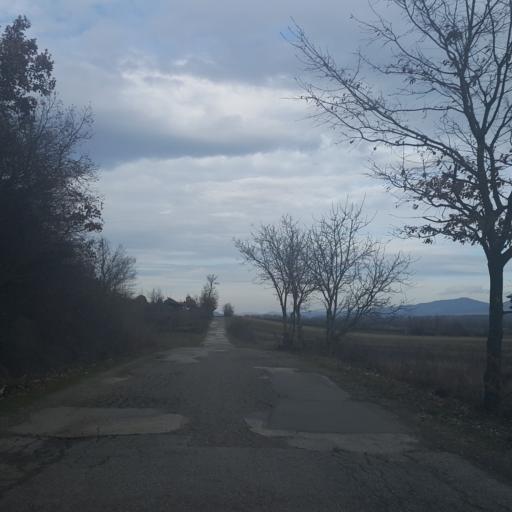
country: RS
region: Central Serbia
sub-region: Zajecarski Okrug
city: Knjazevac
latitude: 43.6105
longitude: 22.2599
